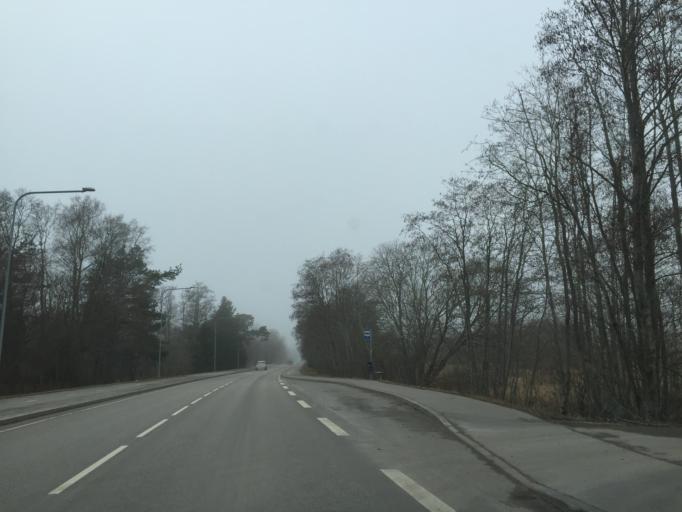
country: EE
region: Saare
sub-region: Kuressaare linn
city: Kuressaare
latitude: 58.2295
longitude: 22.4030
